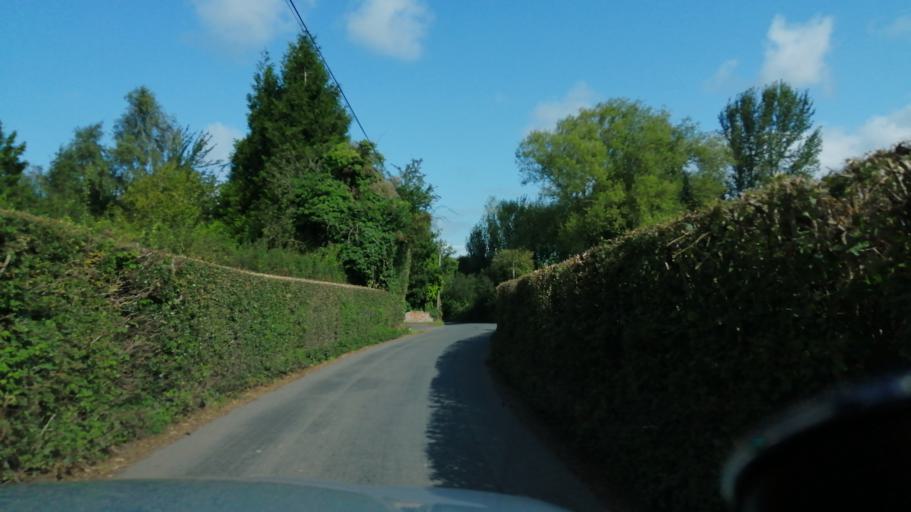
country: GB
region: England
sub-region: Herefordshire
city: Madley
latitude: 52.0509
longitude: -2.8529
